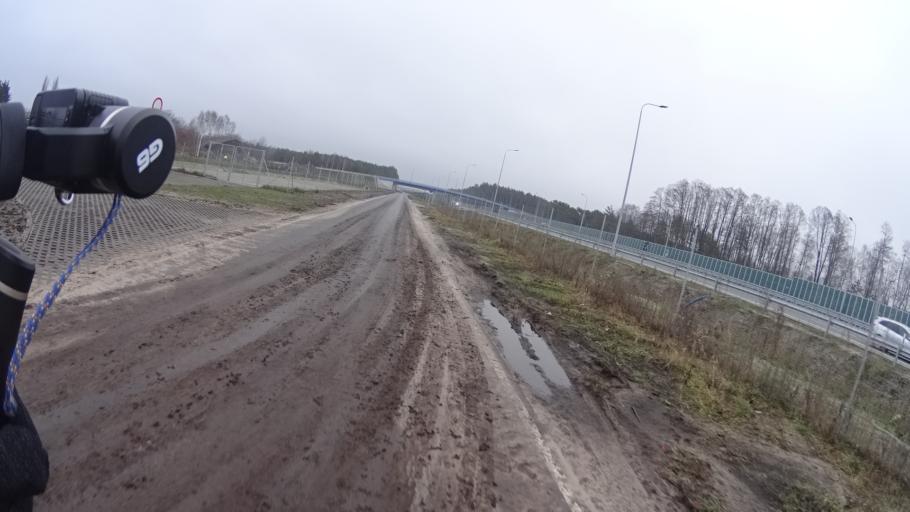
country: PL
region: Masovian Voivodeship
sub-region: Warszawa
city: Wawer
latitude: 52.1659
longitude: 21.1821
